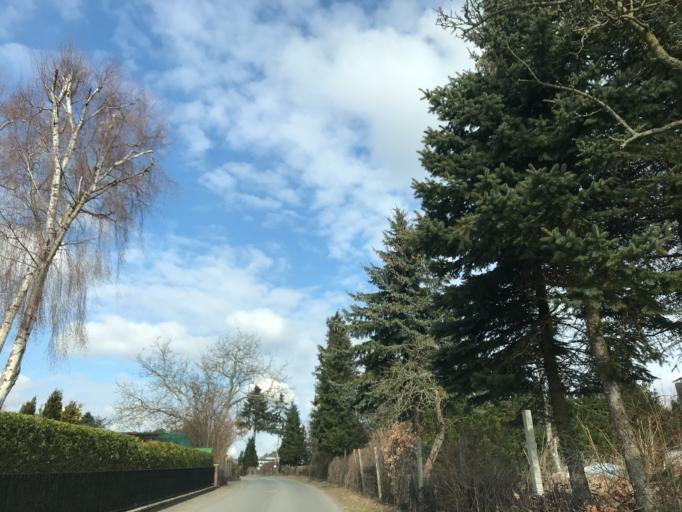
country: DE
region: Berlin
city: Kladow
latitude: 52.4624
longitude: 13.1409
